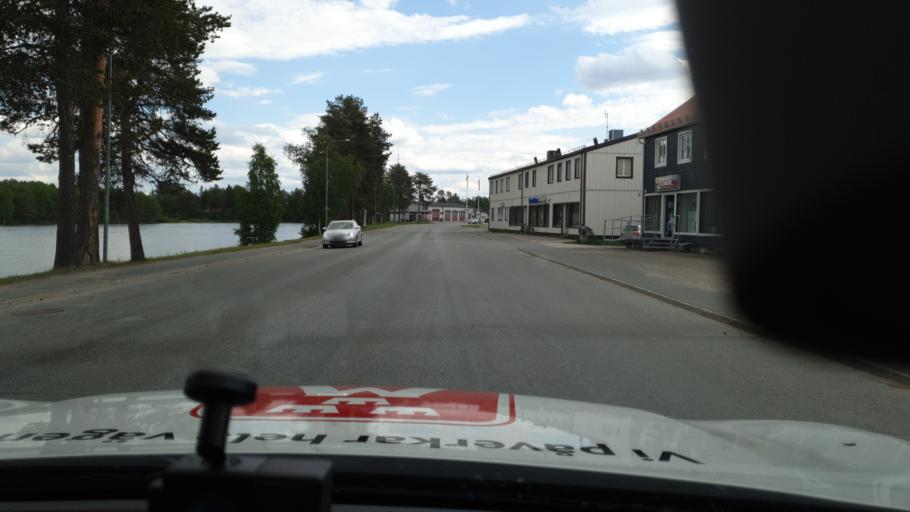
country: SE
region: Vaesterbotten
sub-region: Sorsele Kommun
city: Sorsele
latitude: 65.5379
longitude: 17.5270
